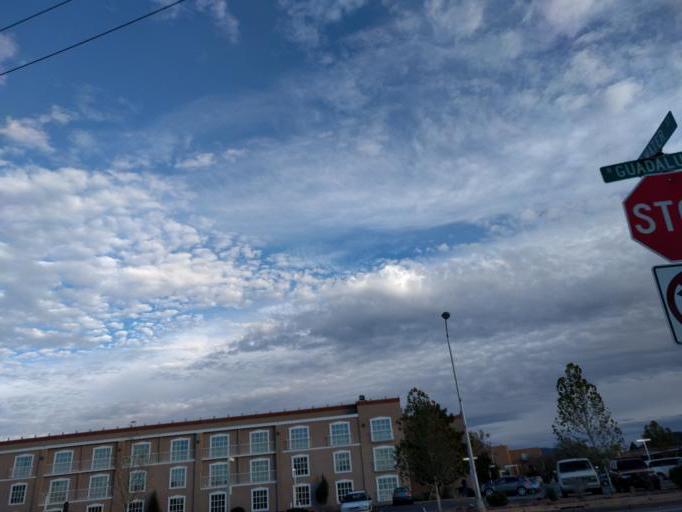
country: US
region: New Mexico
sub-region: Santa Fe County
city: Santa Fe
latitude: 35.6877
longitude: -105.9439
